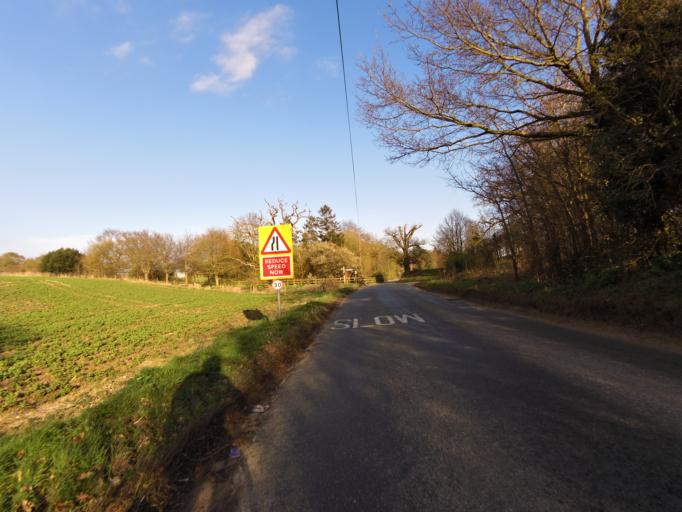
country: GB
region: England
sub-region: Suffolk
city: Kesgrave
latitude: 52.0921
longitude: 1.2359
